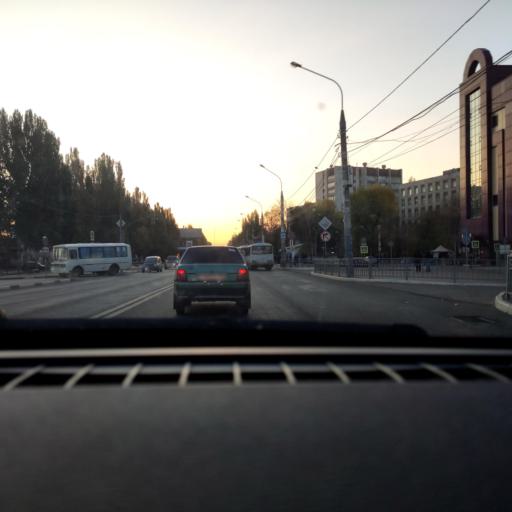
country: RU
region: Voronezj
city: Voronezh
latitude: 51.6721
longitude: 39.2540
